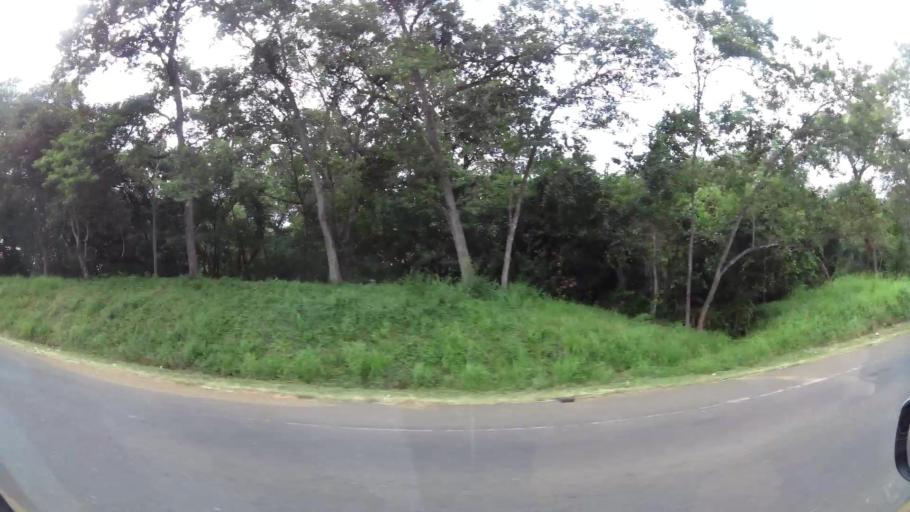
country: CR
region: Alajuela
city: Orotina
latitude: 9.8622
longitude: -84.5746
